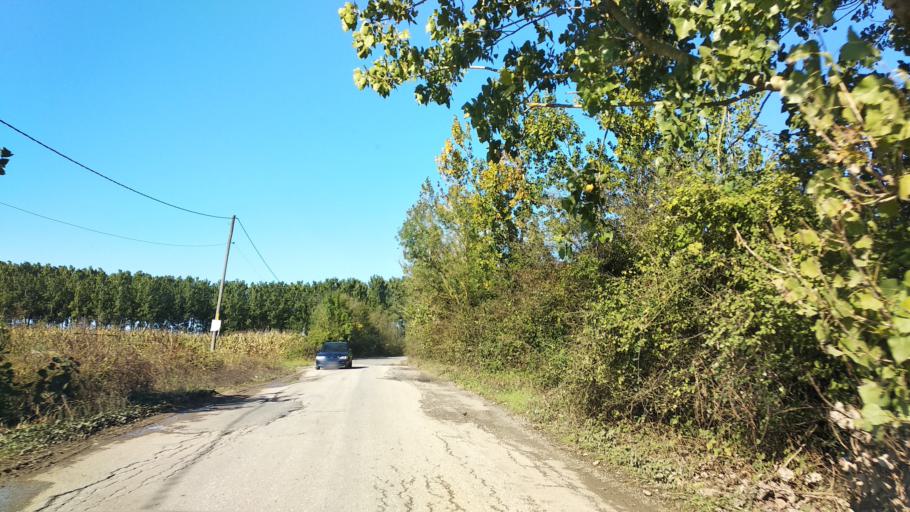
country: TR
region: Sakarya
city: Ortakoy
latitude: 41.0290
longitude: 30.6069
